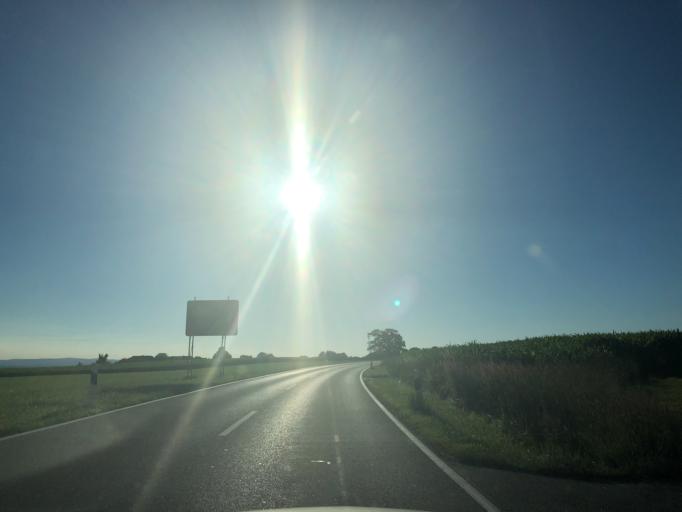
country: DE
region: Bavaria
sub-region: Upper Bavaria
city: Riedering
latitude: 47.8576
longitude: 12.2618
